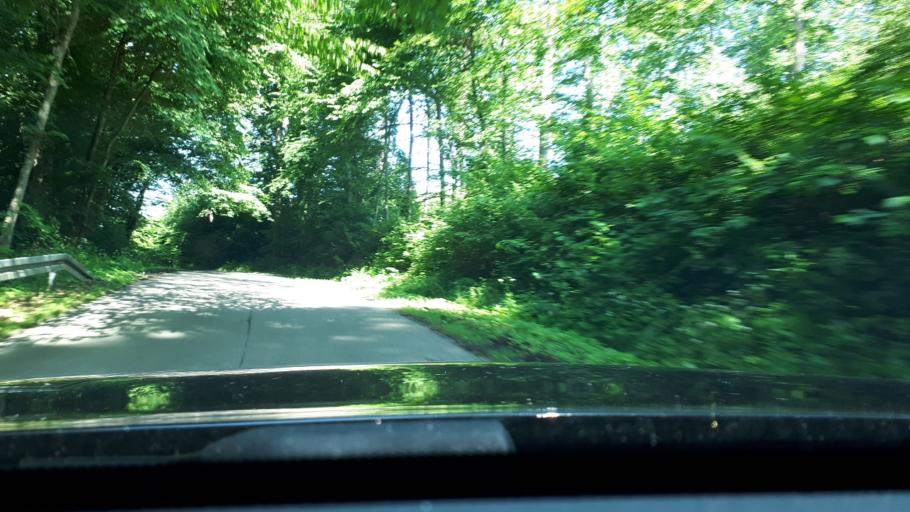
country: PL
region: Warmian-Masurian Voivodeship
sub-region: Powiat ostrodzki
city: Gierzwald
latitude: 53.6369
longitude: 20.0806
